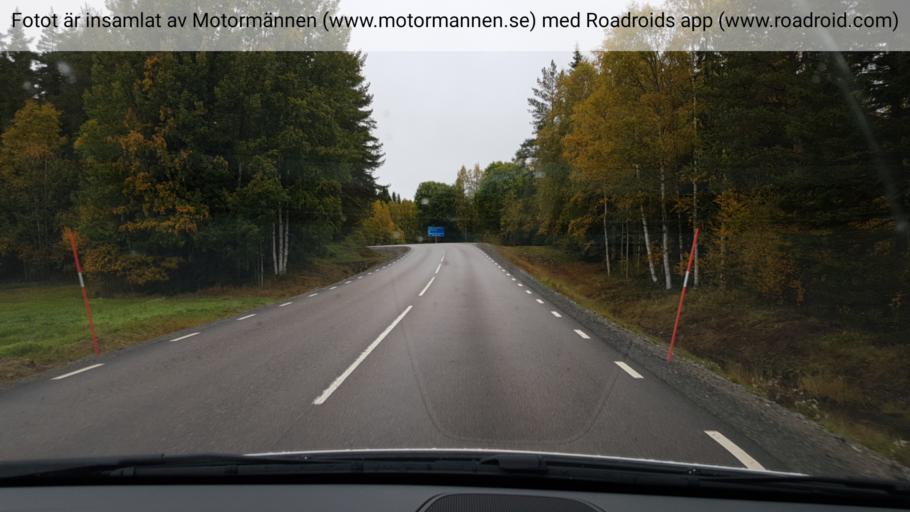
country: SE
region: Vaesterbotten
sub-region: Umea Kommun
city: Ersmark
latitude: 63.9413
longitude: 20.3045
